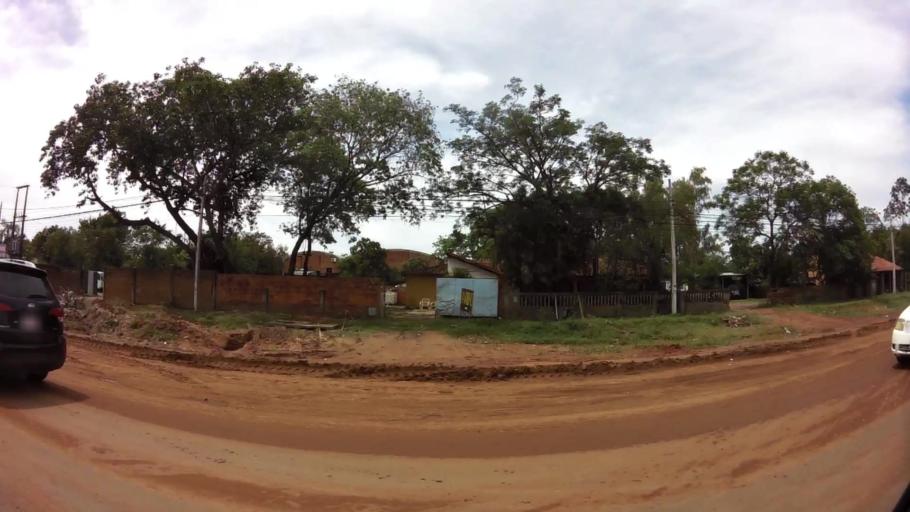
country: PY
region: Central
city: Limpio
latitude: -25.1950
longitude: -57.5103
